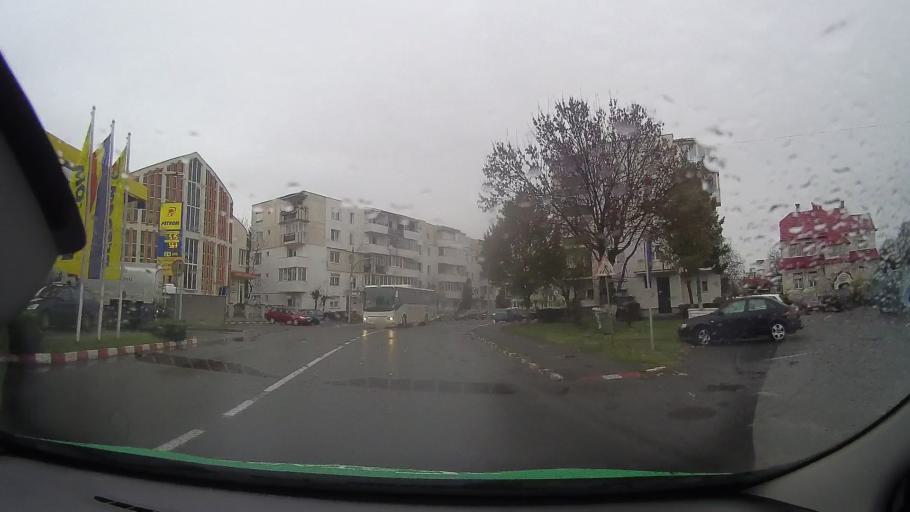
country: RO
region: Mures
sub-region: Municipiul Reghin
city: Reghin
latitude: 46.7797
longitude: 24.7077
